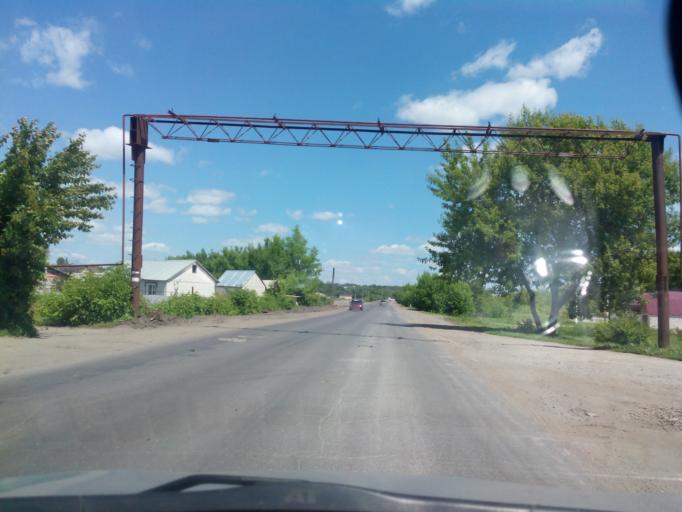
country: RU
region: Tambov
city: Zherdevka
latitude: 51.8121
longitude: 41.5046
